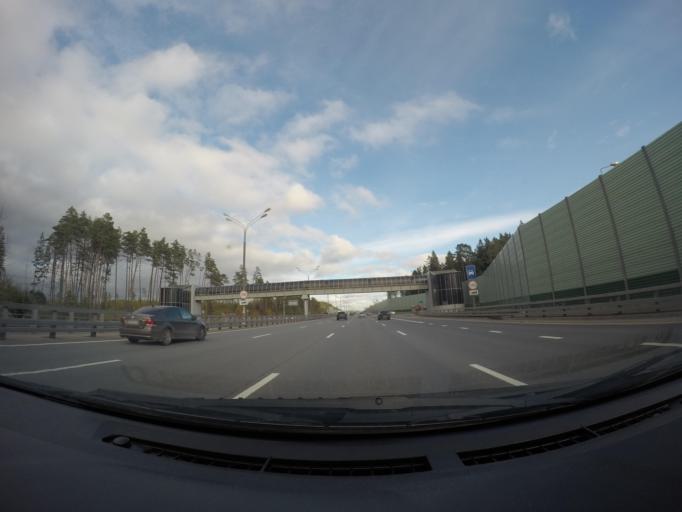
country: RU
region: Moskovskaya
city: Zhavoronki
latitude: 55.6175
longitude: 37.1062
